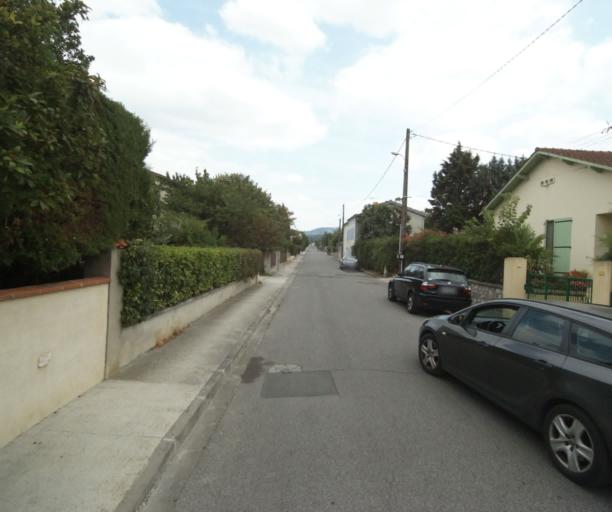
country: FR
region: Midi-Pyrenees
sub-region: Departement de la Haute-Garonne
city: Revel
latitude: 43.4543
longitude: 2.0081
